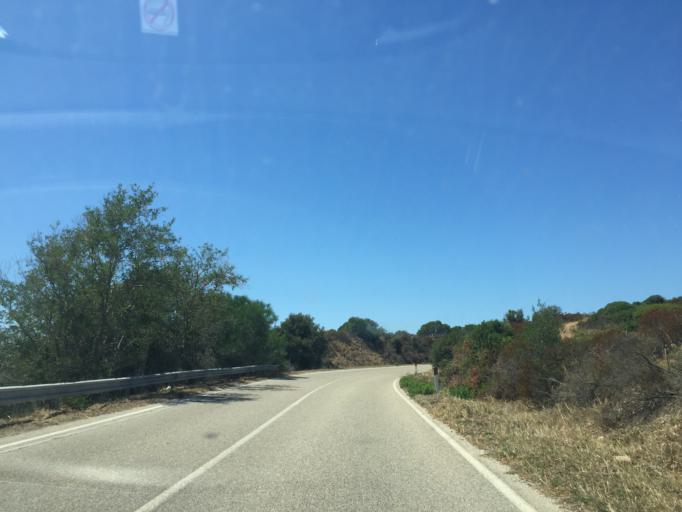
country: IT
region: Sardinia
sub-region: Provincia di Olbia-Tempio
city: Aglientu
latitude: 41.0991
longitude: 9.0841
